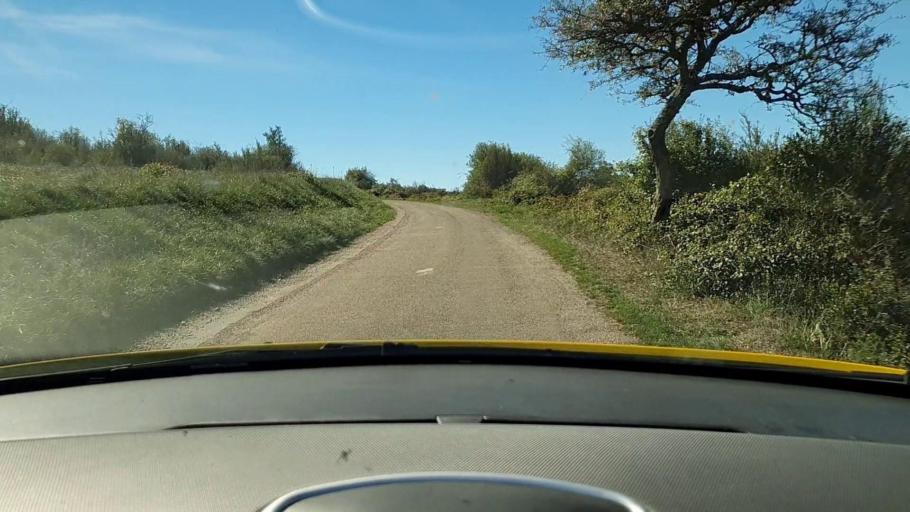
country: FR
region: Languedoc-Roussillon
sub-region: Departement du Gard
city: Aveze
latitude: 43.9600
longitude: 3.4251
